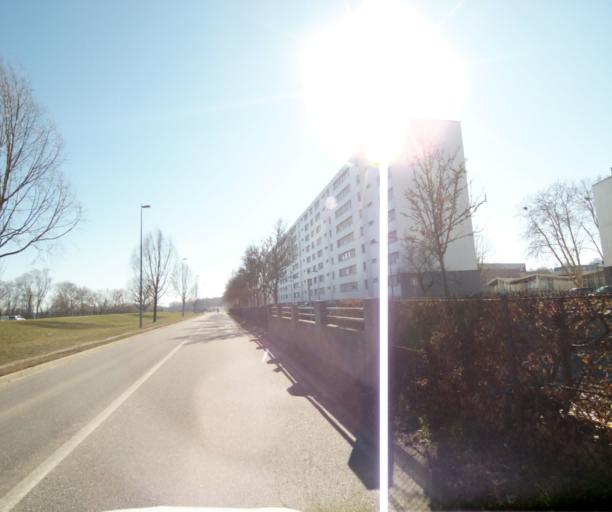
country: FR
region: Lorraine
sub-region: Departement de Meurthe-et-Moselle
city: Jarville-la-Malgrange
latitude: 48.6729
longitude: 6.2091
